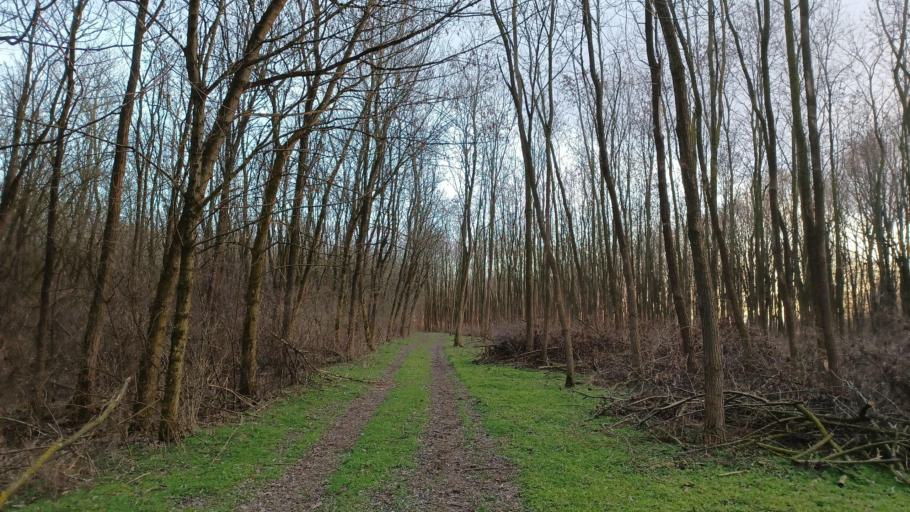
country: HU
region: Tolna
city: Tengelic
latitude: 46.5355
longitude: 18.6989
